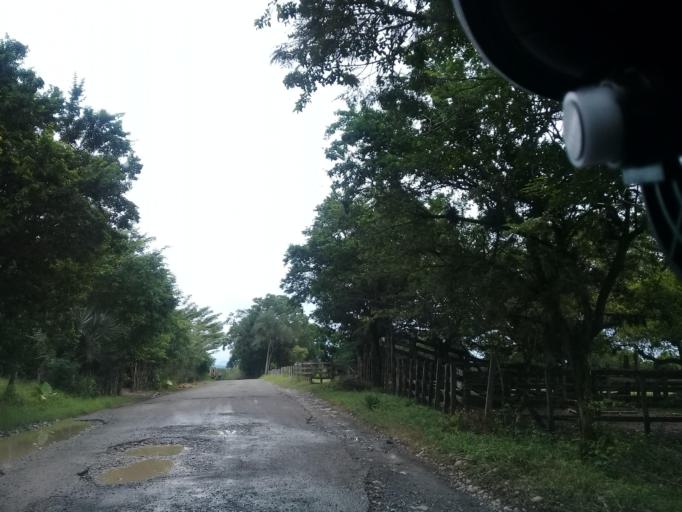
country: MX
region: Hidalgo
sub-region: Huejutla de Reyes
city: Chalahuiyapa
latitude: 21.1893
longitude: -98.3101
